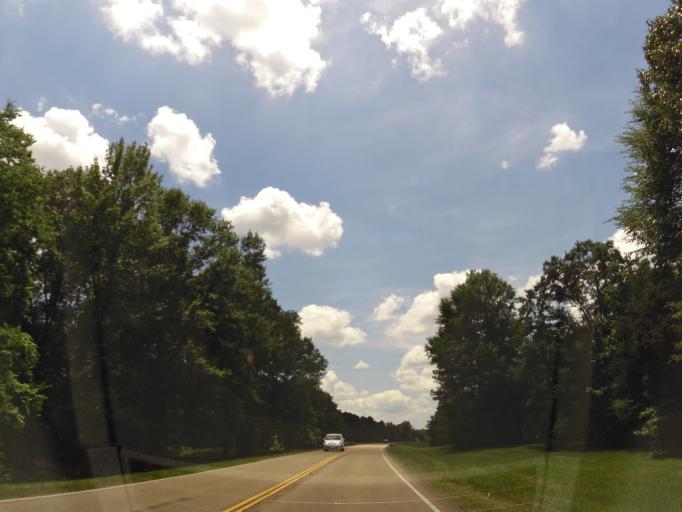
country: US
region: Mississippi
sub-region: Lee County
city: Tupelo
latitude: 34.2830
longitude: -88.7317
